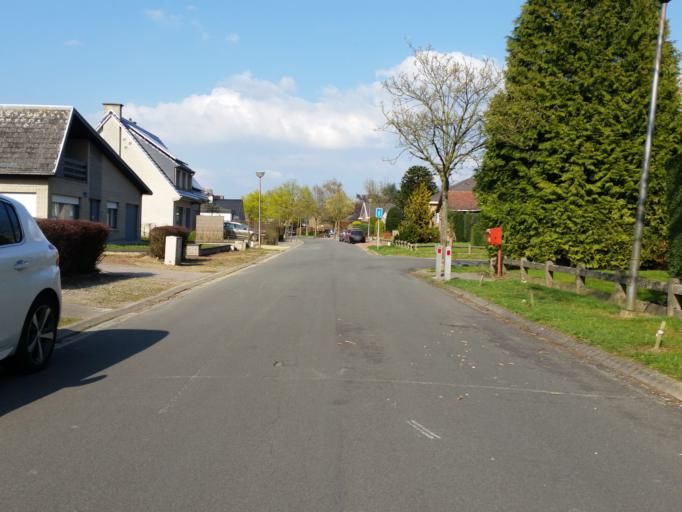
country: BE
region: Flanders
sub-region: Provincie Vlaams-Brabant
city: Zemst
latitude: 50.9724
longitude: 4.5011
